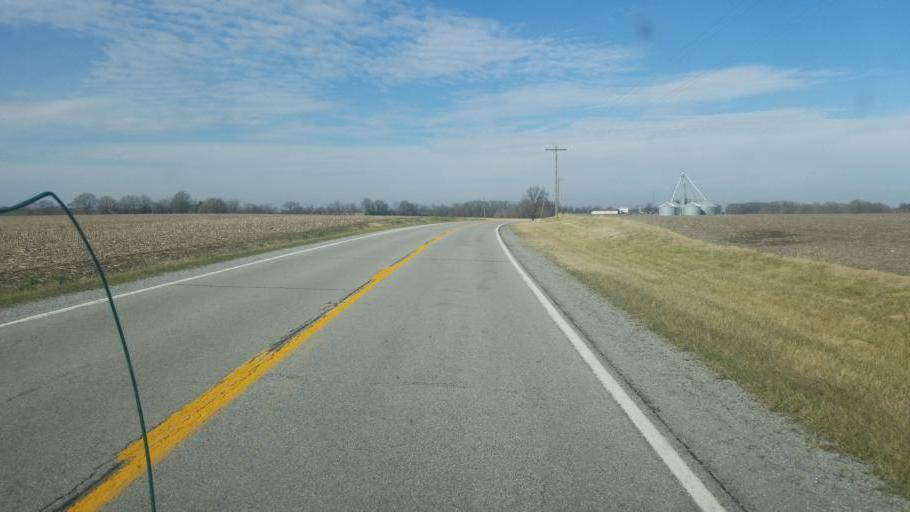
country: US
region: Illinois
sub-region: Saline County
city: Eldorado
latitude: 37.9140
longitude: -88.4566
